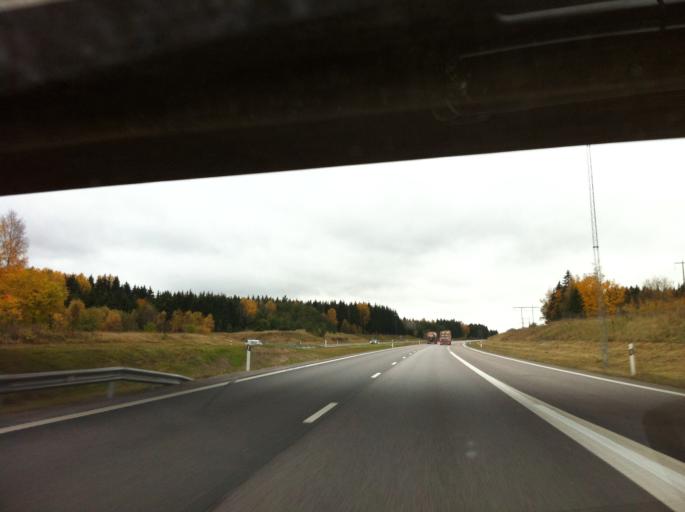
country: SE
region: OEstergoetland
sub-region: Vadstena Kommun
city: Herrestad
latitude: 58.2953
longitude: 14.9241
